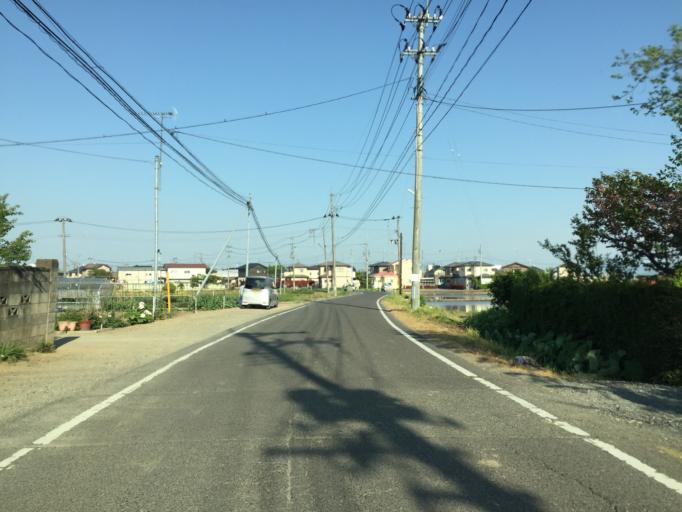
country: JP
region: Fukushima
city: Koriyama
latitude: 37.4063
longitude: 140.3265
